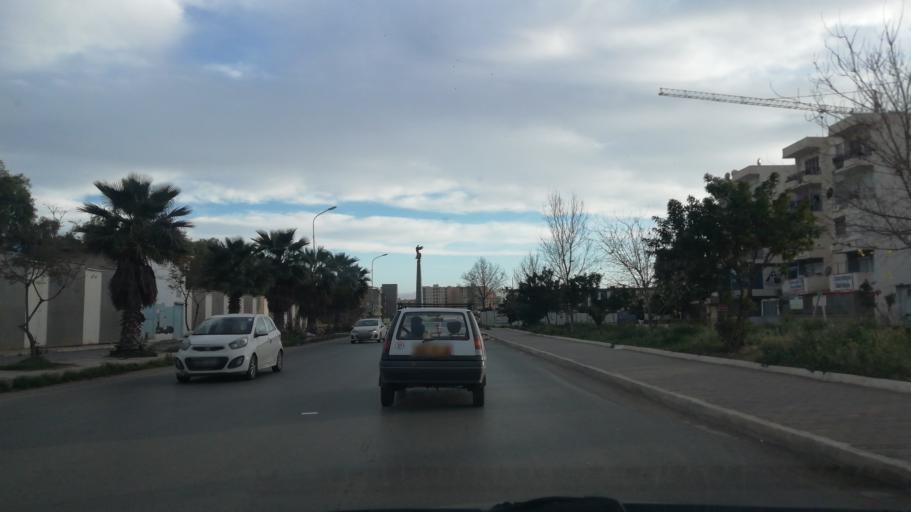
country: DZ
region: Oran
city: Bir el Djir
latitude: 35.6982
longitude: -0.5852
